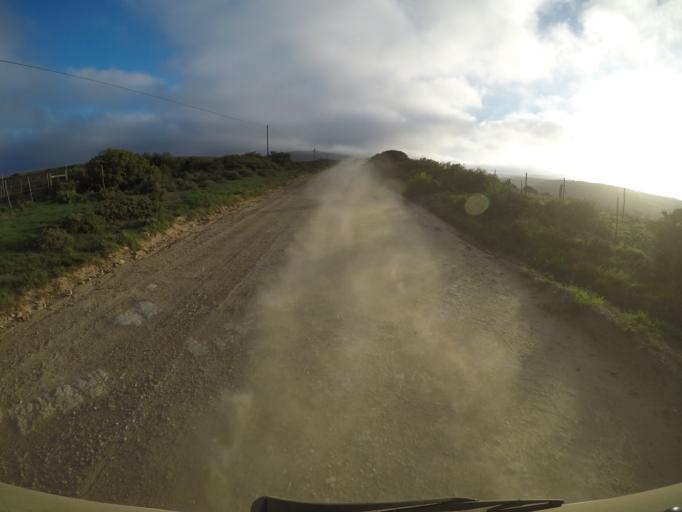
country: ZA
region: Western Cape
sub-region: Eden District Municipality
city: Mossel Bay
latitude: -34.1325
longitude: 22.0448
